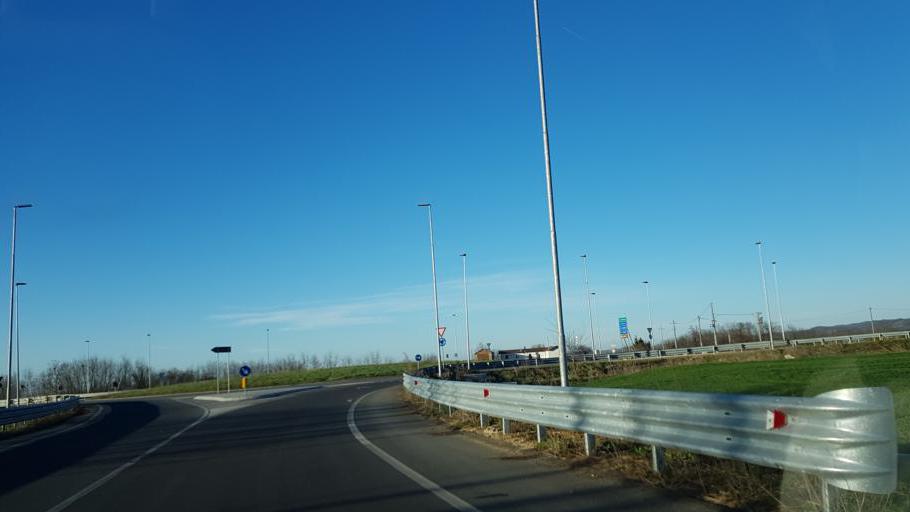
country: IT
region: Piedmont
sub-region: Provincia di Alessandria
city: Serravalle Scrivia
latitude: 44.7433
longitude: 8.8349
